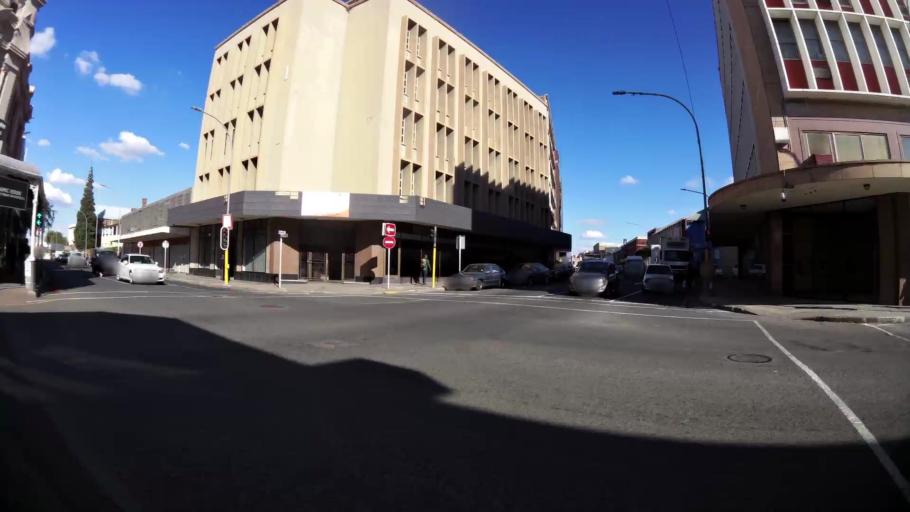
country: ZA
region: Northern Cape
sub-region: Frances Baard District Municipality
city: Kimberley
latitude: -28.7403
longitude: 24.7650
